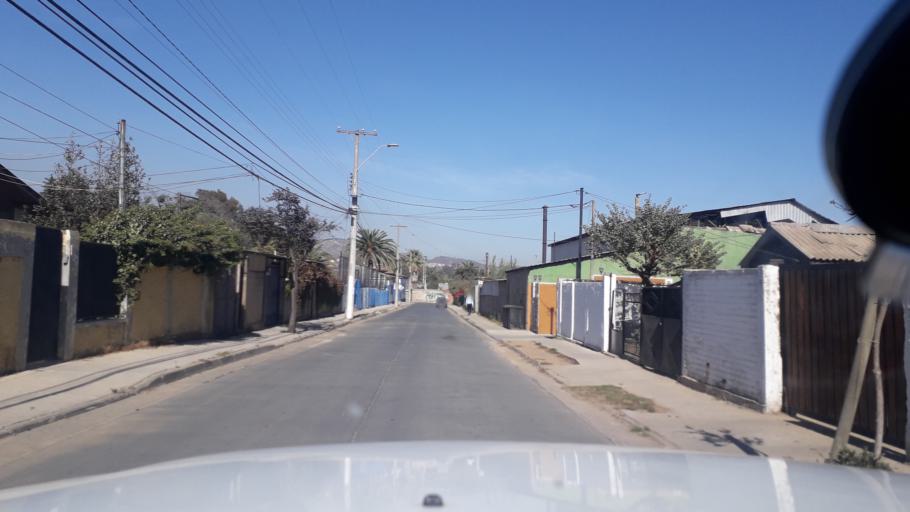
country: CL
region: Valparaiso
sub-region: Provincia de Marga Marga
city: Villa Alemana
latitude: -33.0388
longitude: -71.3549
